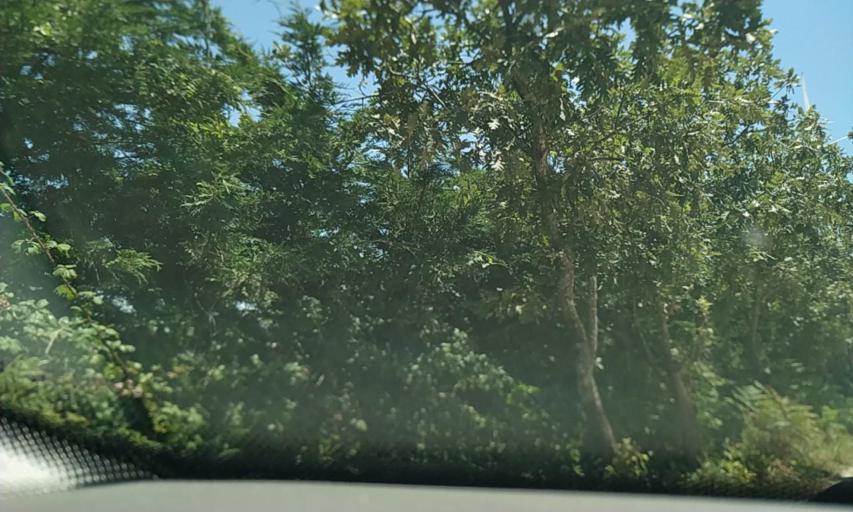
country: PT
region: Lisbon
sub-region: Sintra
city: Almargem
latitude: 38.8420
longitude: -9.2678
